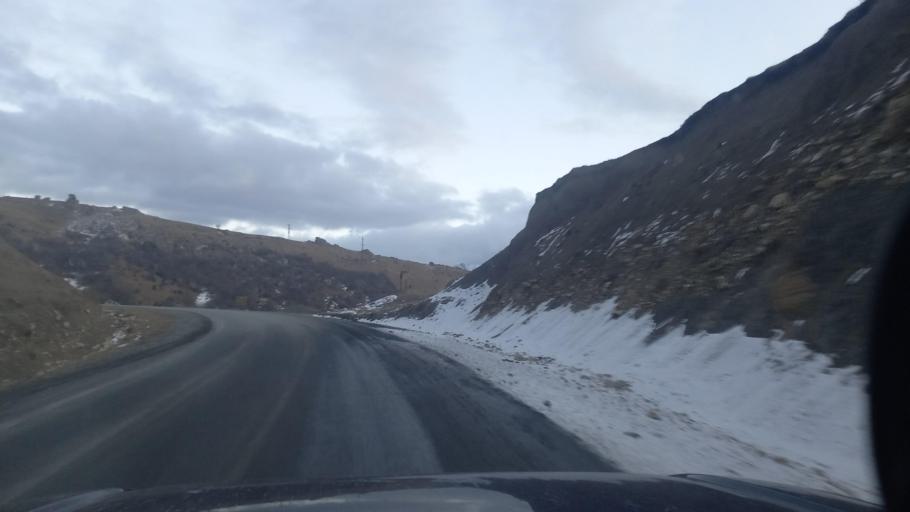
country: RU
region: Ingushetiya
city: Dzhayrakh
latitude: 42.8215
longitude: 44.8212
